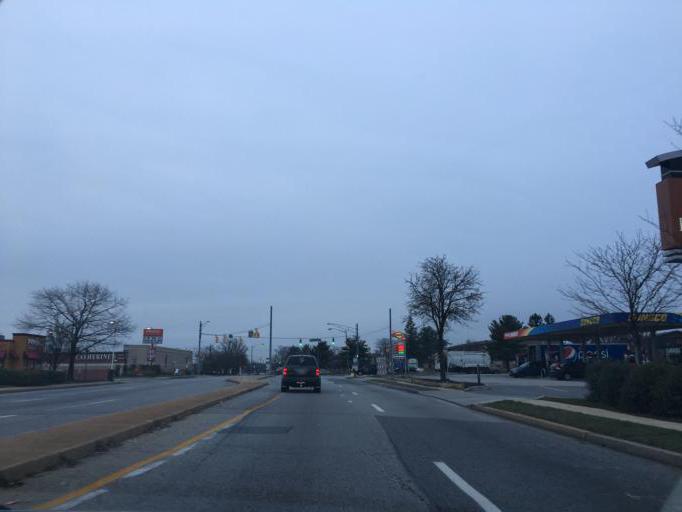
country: US
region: Maryland
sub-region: Baltimore County
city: Woodlawn
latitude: 39.3127
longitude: -76.7552
